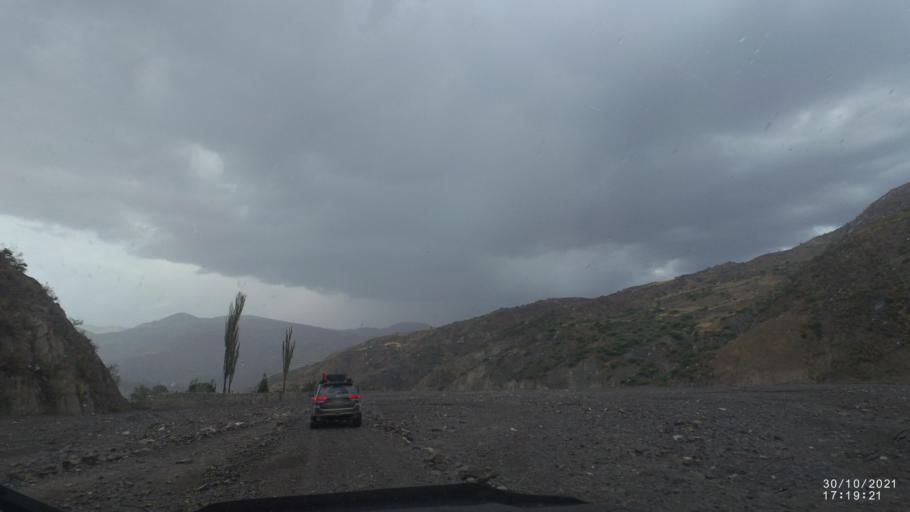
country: BO
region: Cochabamba
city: Colchani
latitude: -17.5341
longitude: -66.6212
